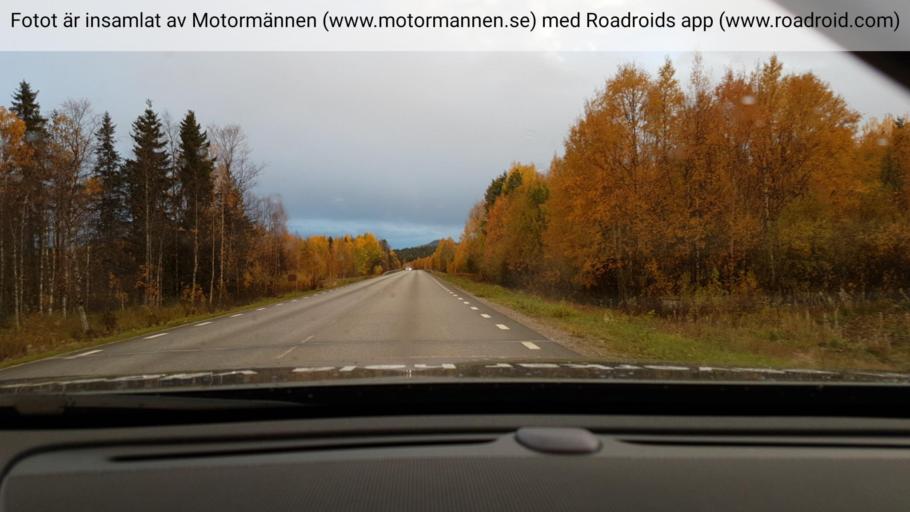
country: SE
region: Norrbotten
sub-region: Overkalix Kommun
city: OEverkalix
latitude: 66.3592
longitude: 22.8343
